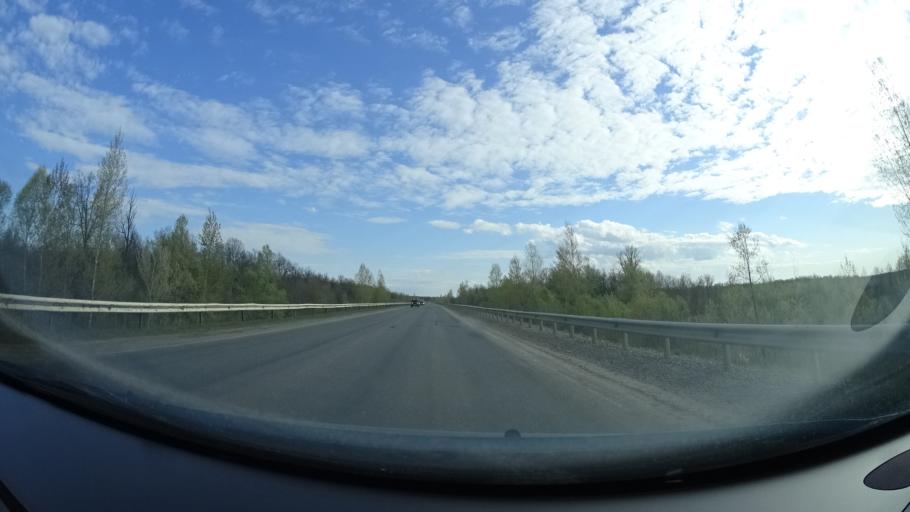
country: RU
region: Bashkortostan
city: Blagoveshchensk
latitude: 55.0355
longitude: 55.8033
